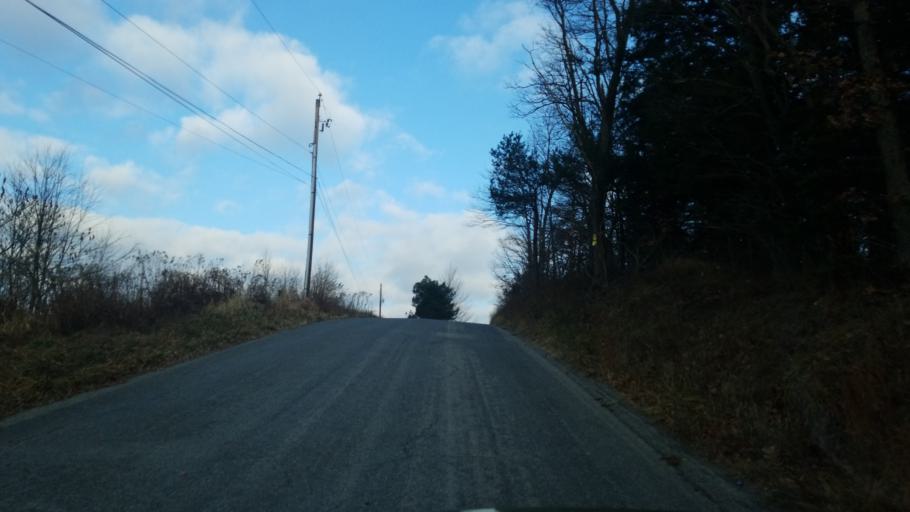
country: US
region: Pennsylvania
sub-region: Clearfield County
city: Clearfield
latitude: 41.0098
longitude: -78.4208
